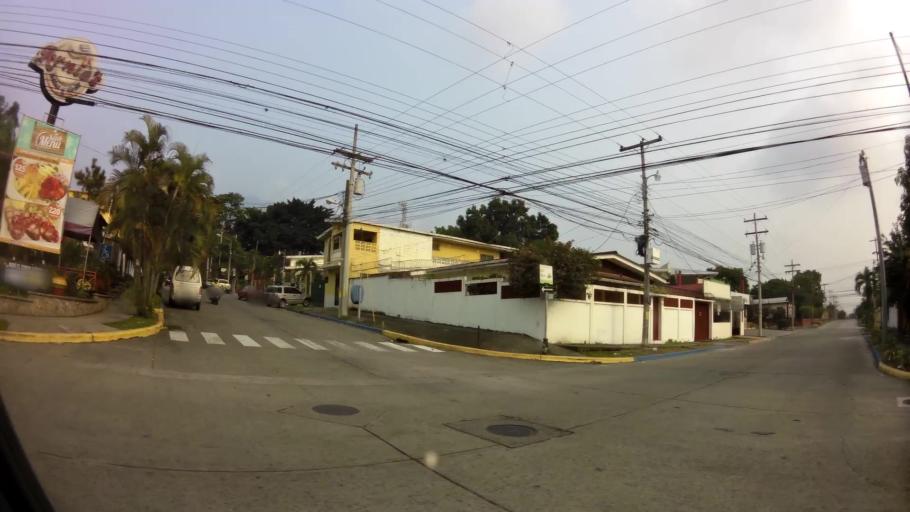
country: HN
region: Cortes
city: Armenta
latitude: 15.5026
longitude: -88.0397
